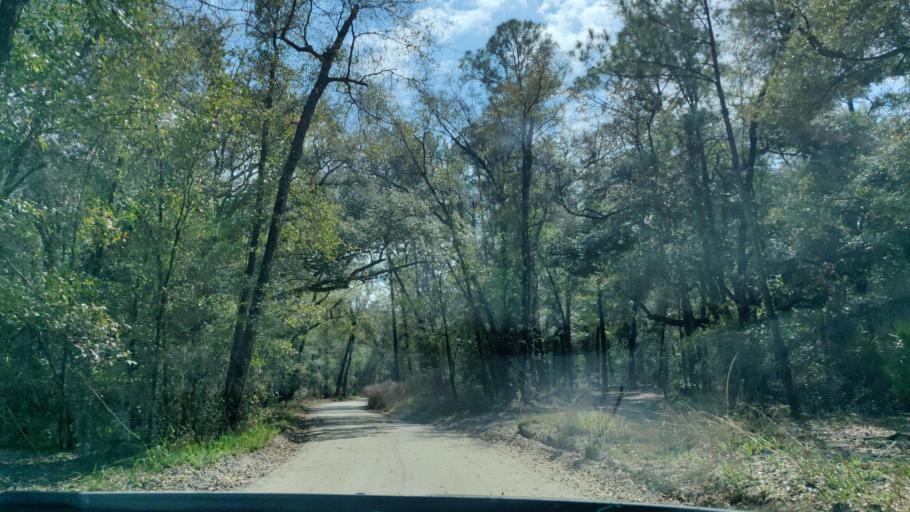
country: US
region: Florida
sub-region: Clay County
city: Middleburg
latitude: 30.1563
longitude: -81.9349
